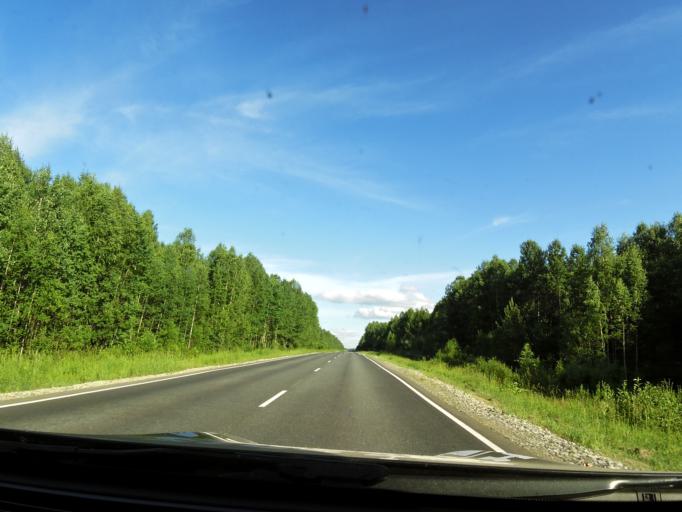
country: RU
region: Kirov
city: Chernaya Kholunitsa
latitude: 58.8030
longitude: 51.8555
